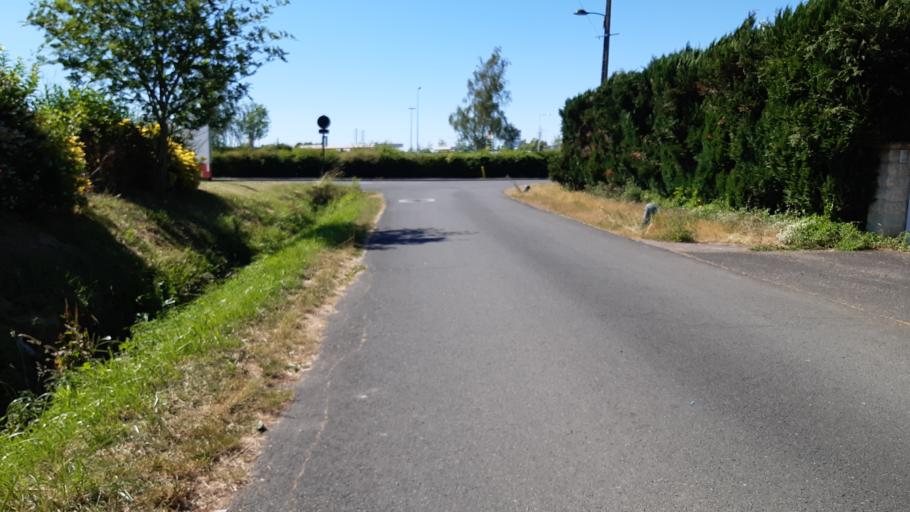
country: FR
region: Centre
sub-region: Departement d'Indre-et-Loire
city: La Membrolle-sur-Choisille
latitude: 47.4274
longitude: 0.6555
